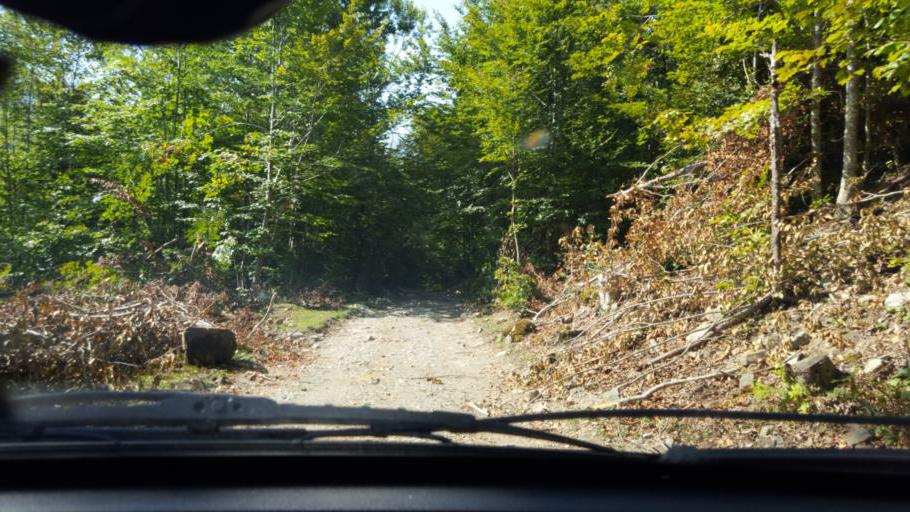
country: ME
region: Andrijevica
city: Andrijevica
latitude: 42.5856
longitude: 19.6323
